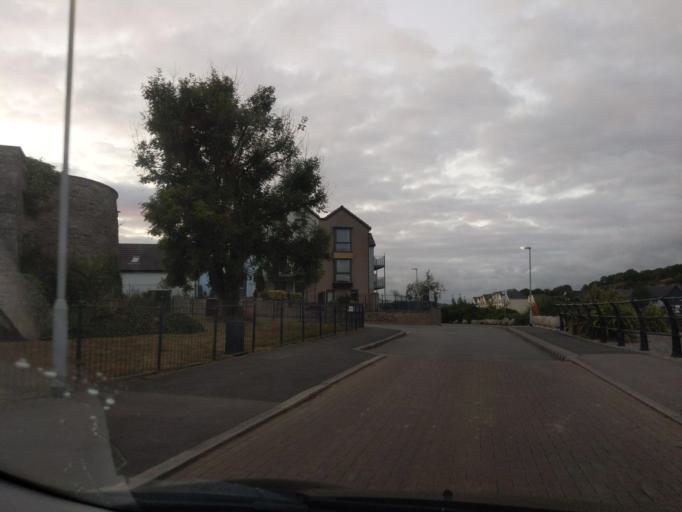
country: GB
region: England
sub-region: Plymouth
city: Plymstock
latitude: 50.3558
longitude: -4.1133
